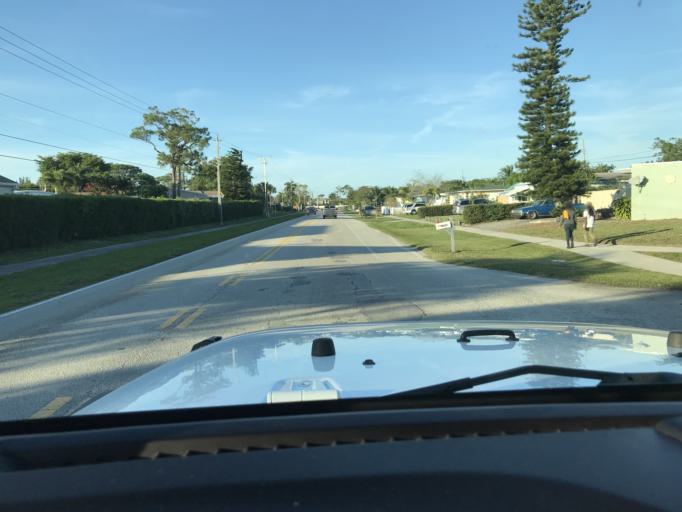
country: US
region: Florida
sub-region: Palm Beach County
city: Seminole Manor
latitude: 26.5842
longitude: -80.1052
